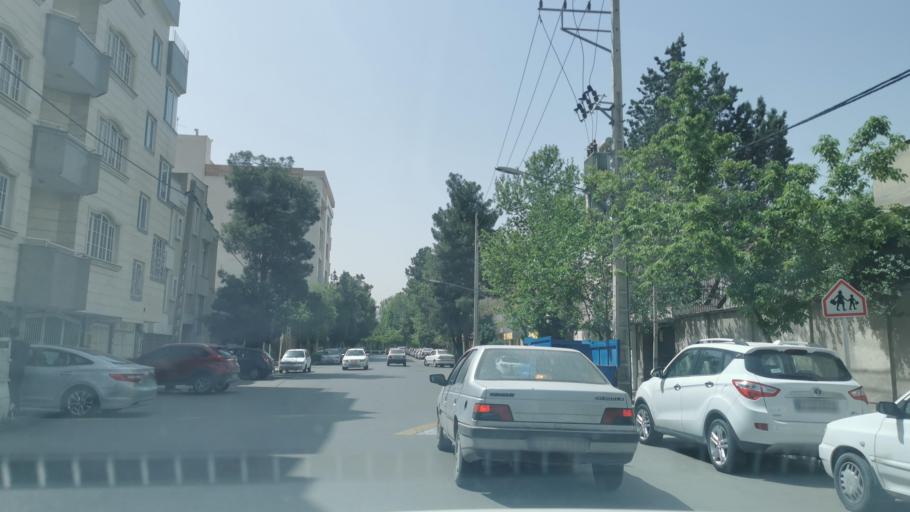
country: IR
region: Razavi Khorasan
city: Mashhad
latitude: 36.3052
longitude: 59.5586
